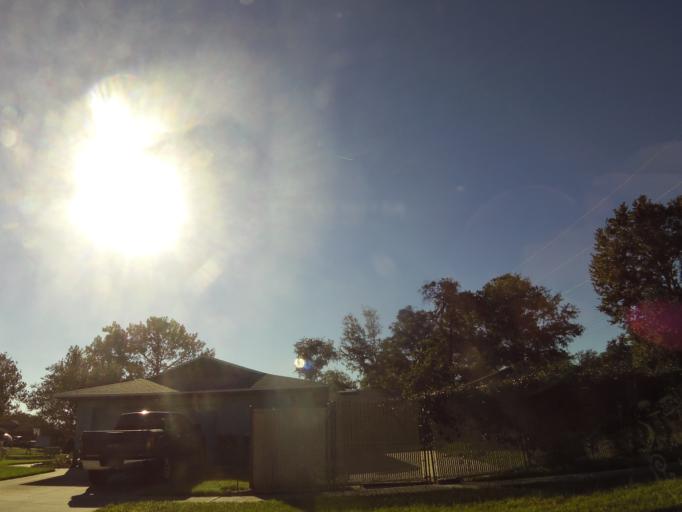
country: US
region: Florida
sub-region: Duval County
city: Neptune Beach
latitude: 30.3036
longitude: -81.4381
